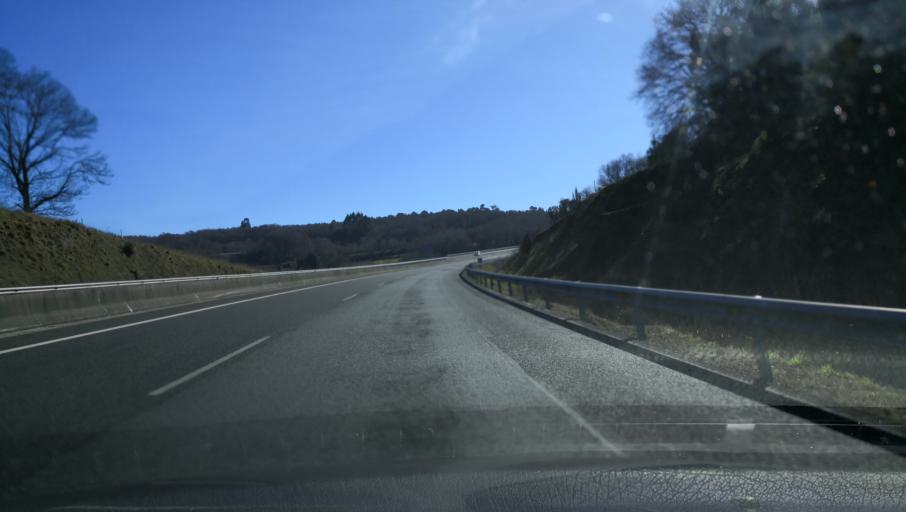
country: ES
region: Galicia
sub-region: Provincia de Pontevedra
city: Lalin
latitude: 42.6312
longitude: -8.1219
